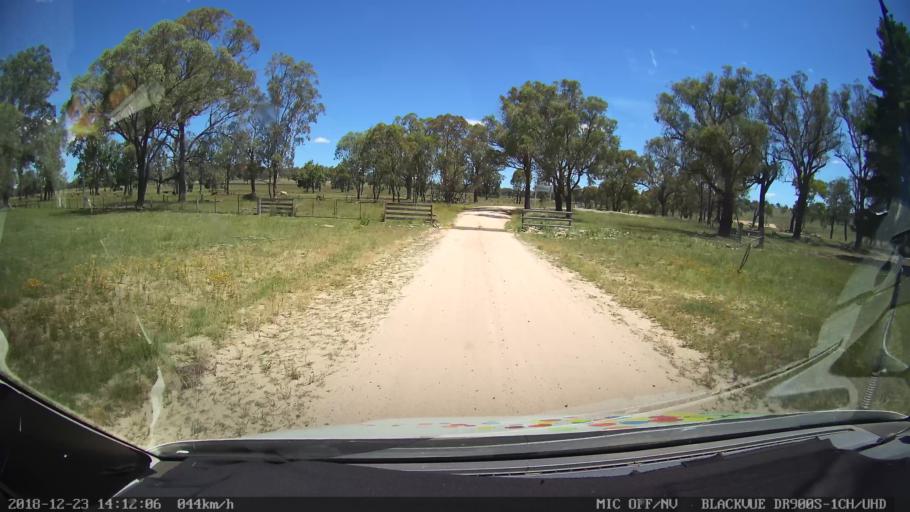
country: AU
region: New South Wales
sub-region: Tamworth Municipality
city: Manilla
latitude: -30.6539
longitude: 151.0467
